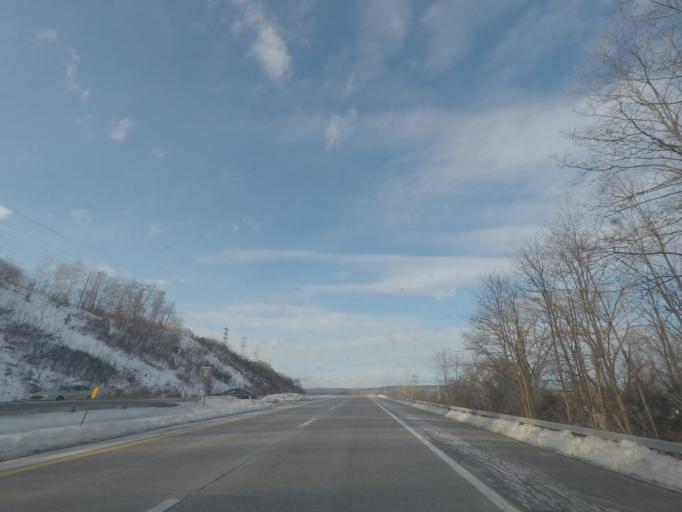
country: US
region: New York
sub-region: Schenectady County
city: Scotia
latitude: 42.8284
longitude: -73.9927
